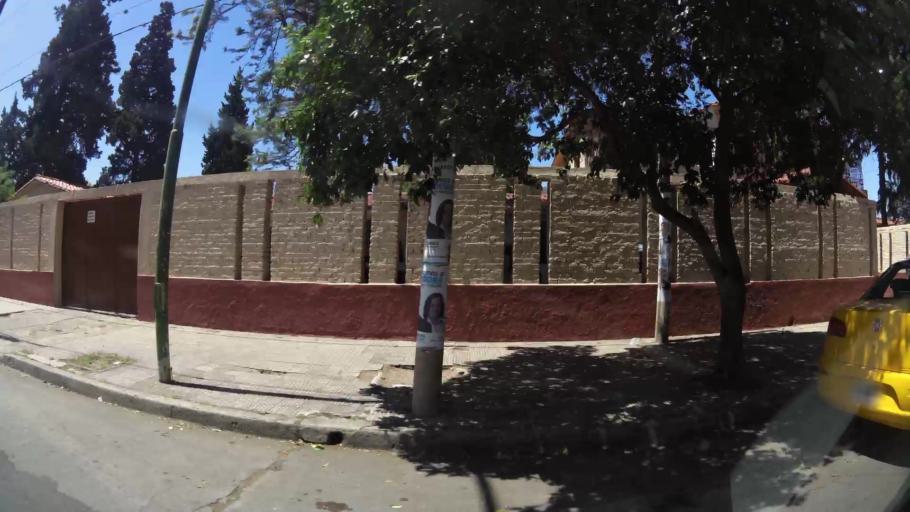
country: AR
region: Cordoba
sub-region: Departamento de Capital
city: Cordoba
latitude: -31.3888
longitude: -64.1602
